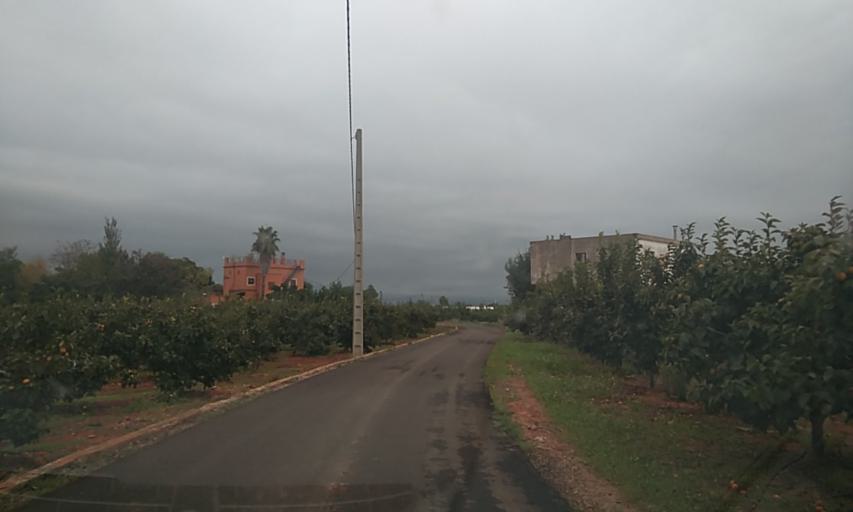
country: ES
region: Valencia
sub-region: Provincia de Valencia
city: Benimodo
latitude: 39.1924
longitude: -0.5599
